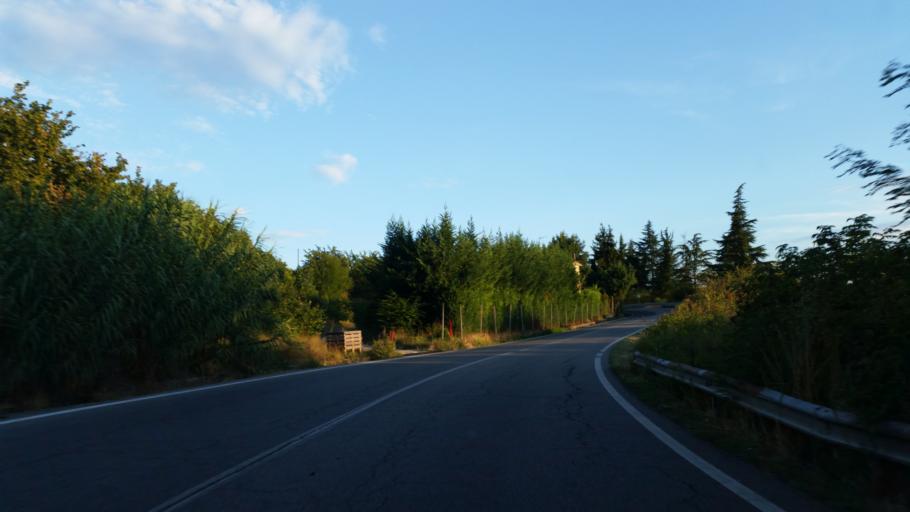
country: IT
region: Piedmont
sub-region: Provincia di Asti
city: Costigliole d'Asti
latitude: 44.8010
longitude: 8.1816
